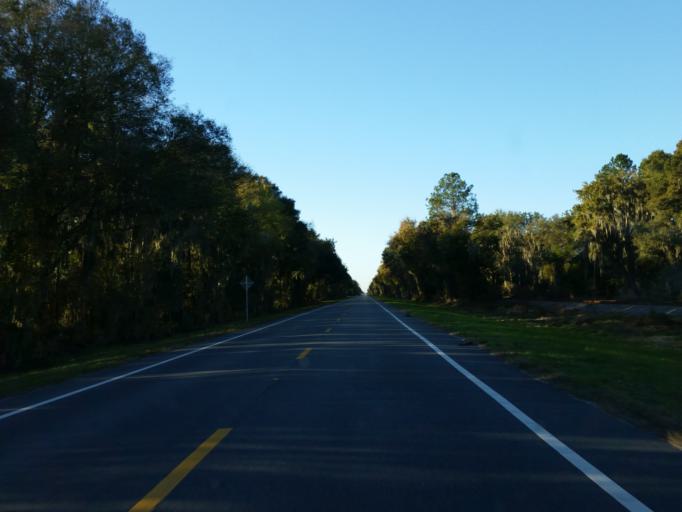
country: US
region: Florida
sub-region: Hamilton County
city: Jasper
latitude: 30.4182
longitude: -82.8535
